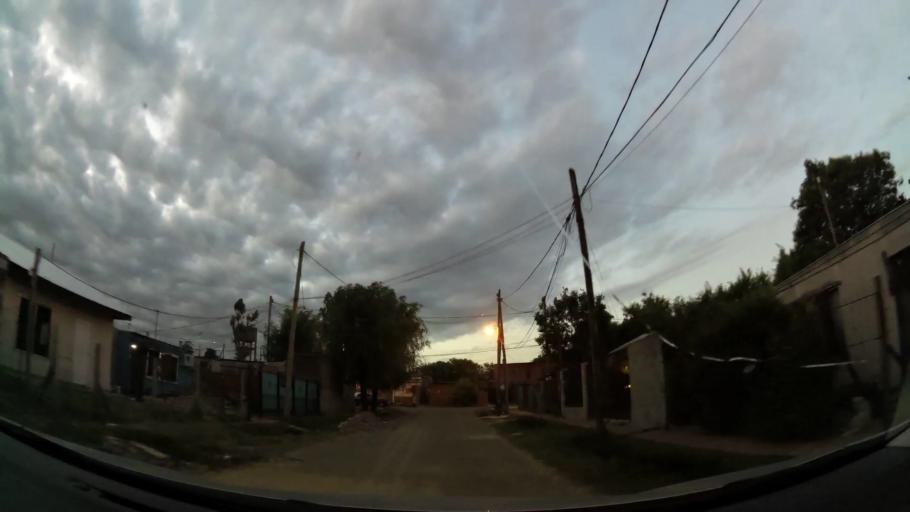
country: AR
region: Buenos Aires
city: Santa Catalina - Dique Lujan
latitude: -34.4153
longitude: -58.6929
